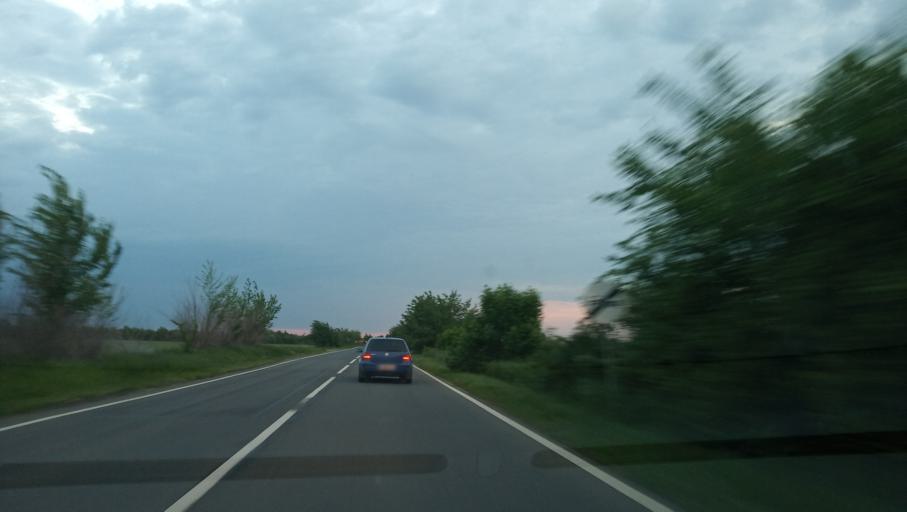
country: RO
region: Timis
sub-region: Comuna Padureni
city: Padureni
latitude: 45.6181
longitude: 21.1947
